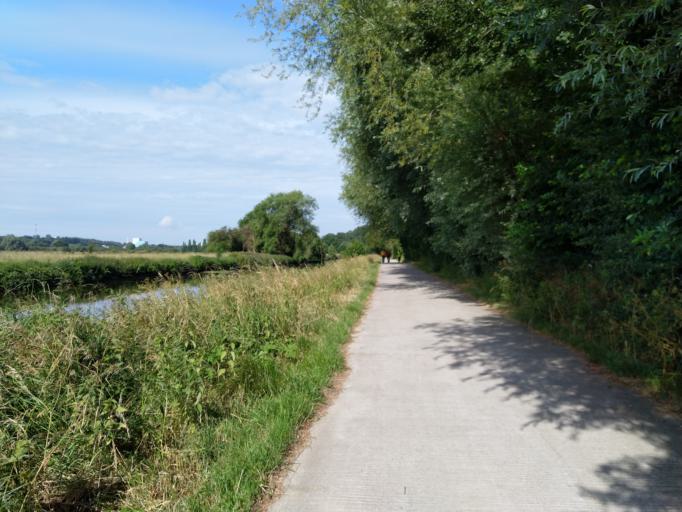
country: FR
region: Nord-Pas-de-Calais
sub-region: Departement du Nord
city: Rousies
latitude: 50.2850
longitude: 4.0109
